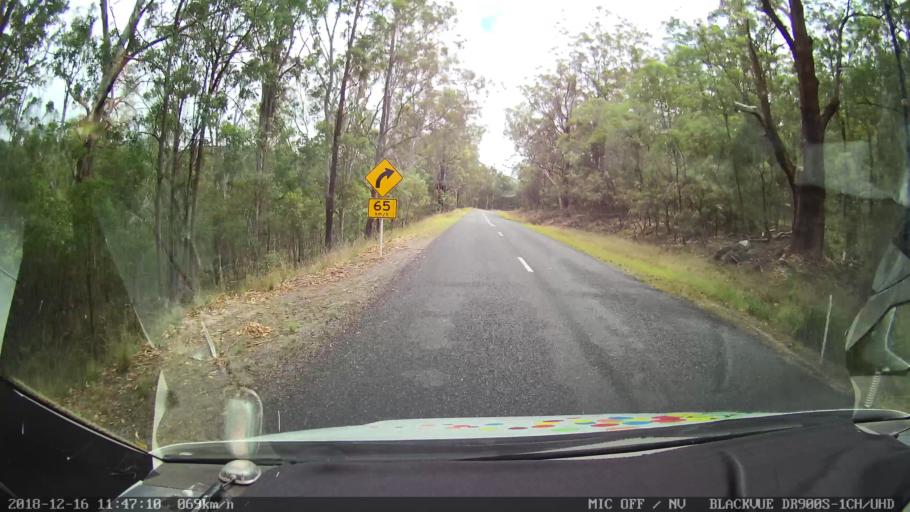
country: AU
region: New South Wales
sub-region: Tenterfield Municipality
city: Carrolls Creek
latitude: -28.9231
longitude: 152.2357
